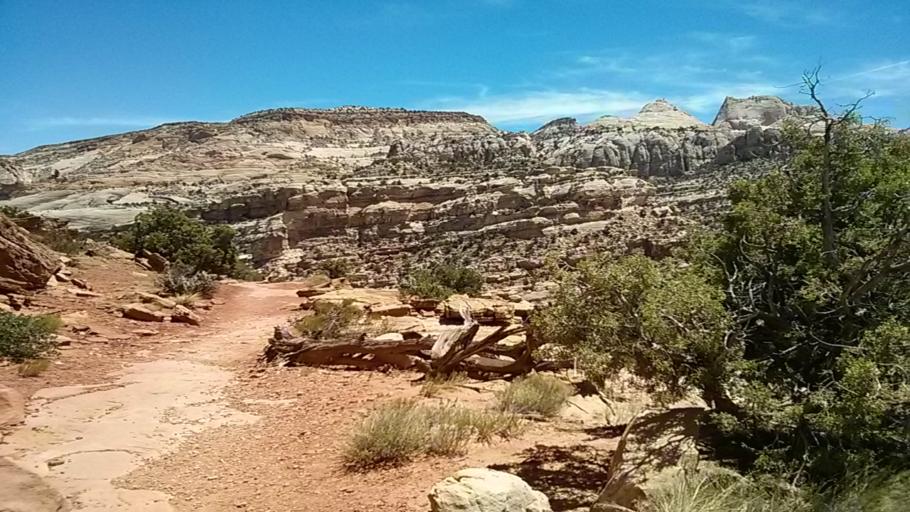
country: US
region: Utah
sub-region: Wayne County
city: Loa
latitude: 38.2635
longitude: -111.2218
